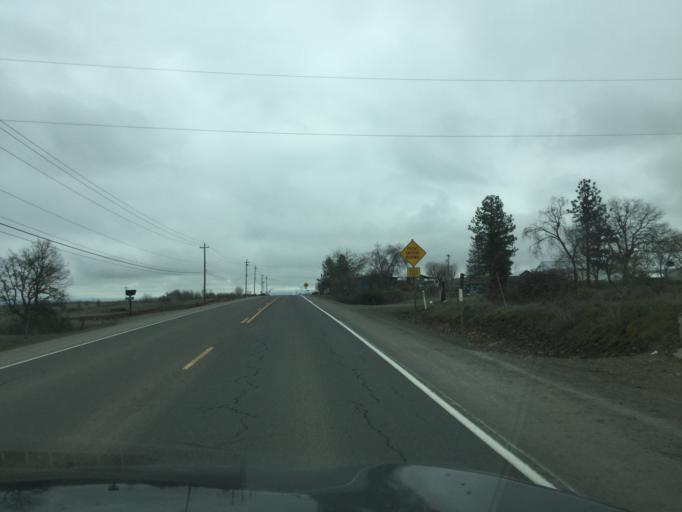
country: US
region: Oregon
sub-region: Jackson County
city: Central Point
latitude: 42.4283
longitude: -122.9390
